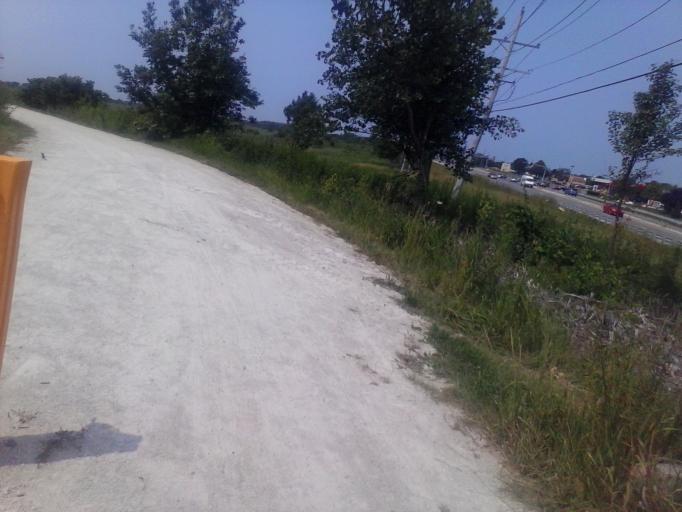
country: US
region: Illinois
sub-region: DuPage County
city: Lisle
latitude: 41.8289
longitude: -88.0940
